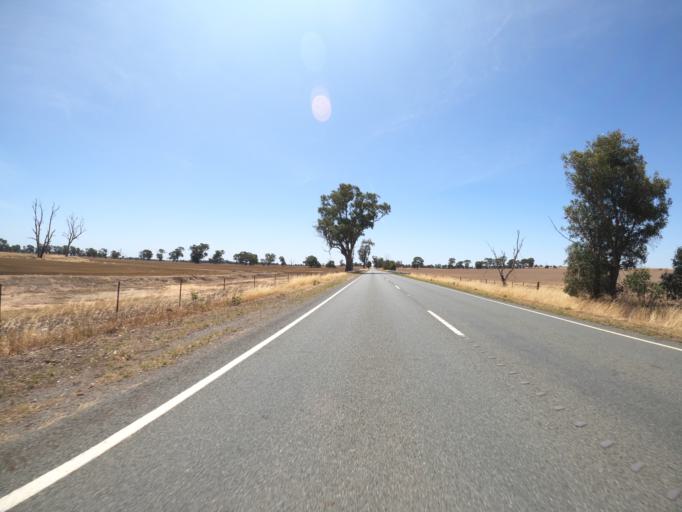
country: AU
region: Victoria
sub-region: Moira
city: Yarrawonga
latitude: -36.0591
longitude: 145.9954
